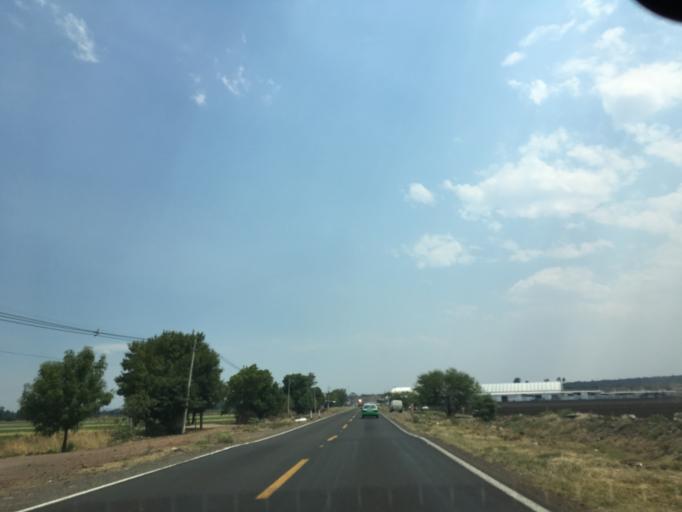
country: MX
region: Guanajuato
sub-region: Moroleon
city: Rinconadas del Bosque
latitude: 20.0765
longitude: -101.1561
